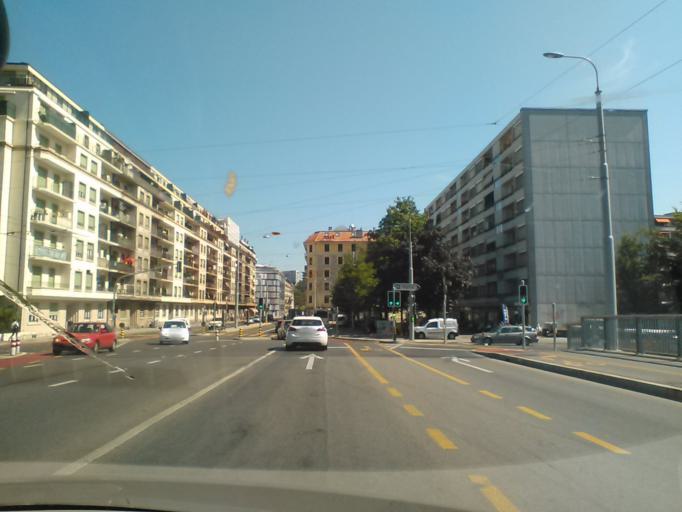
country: CH
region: Geneva
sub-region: Geneva
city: Lancy
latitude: 46.1994
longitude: 6.1286
